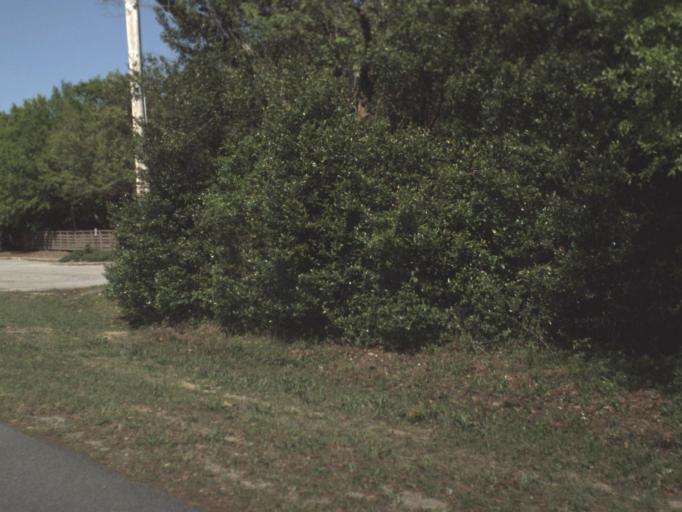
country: US
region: Florida
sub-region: Escambia County
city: East Pensacola Heights
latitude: 30.4518
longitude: -87.1712
